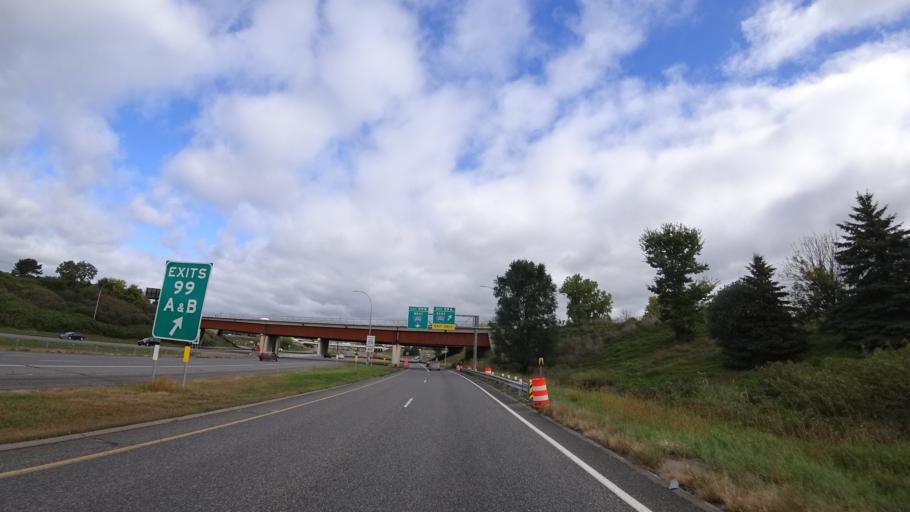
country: US
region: Minnesota
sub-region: Dakota County
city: Mendota Heights
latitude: 44.8570
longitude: -93.1461
